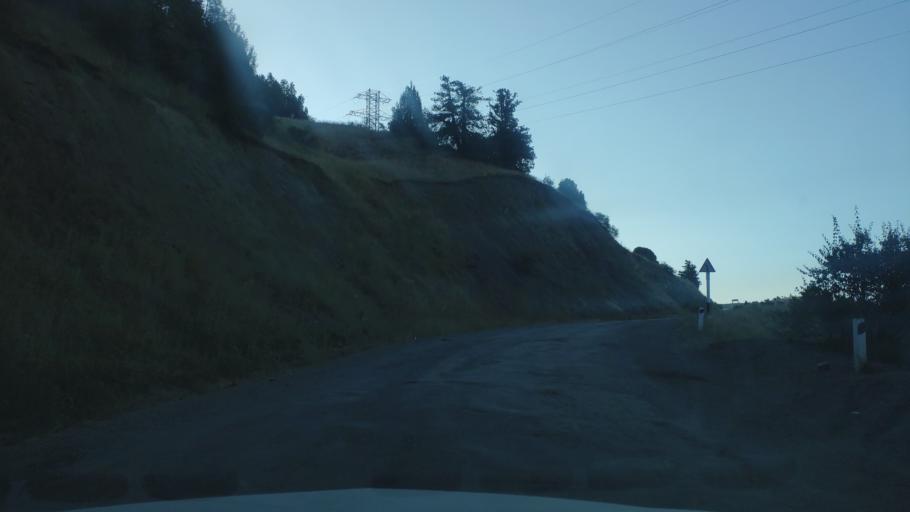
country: TJ
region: Viloyati Sughd
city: Ayni
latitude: 39.6378
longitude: 68.4765
